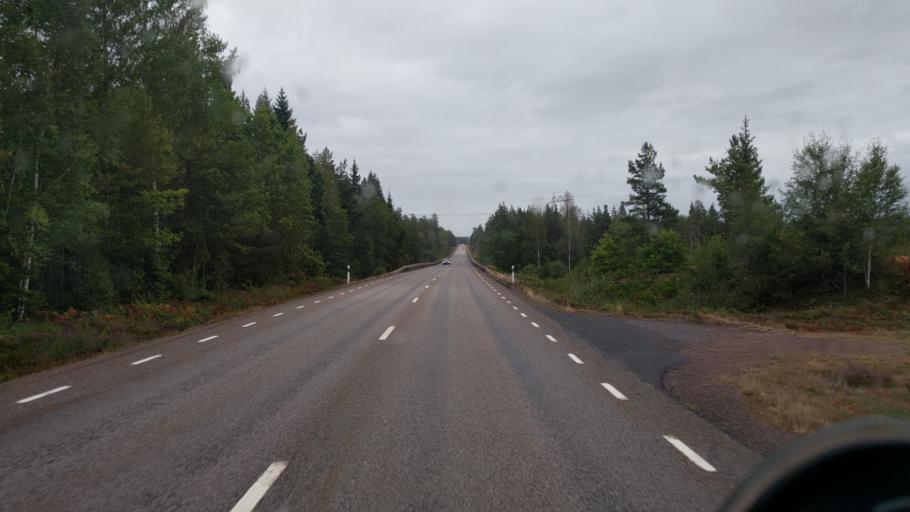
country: SE
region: Kalmar
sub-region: Vasterviks Kommun
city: Ankarsrum
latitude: 57.7006
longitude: 16.2469
